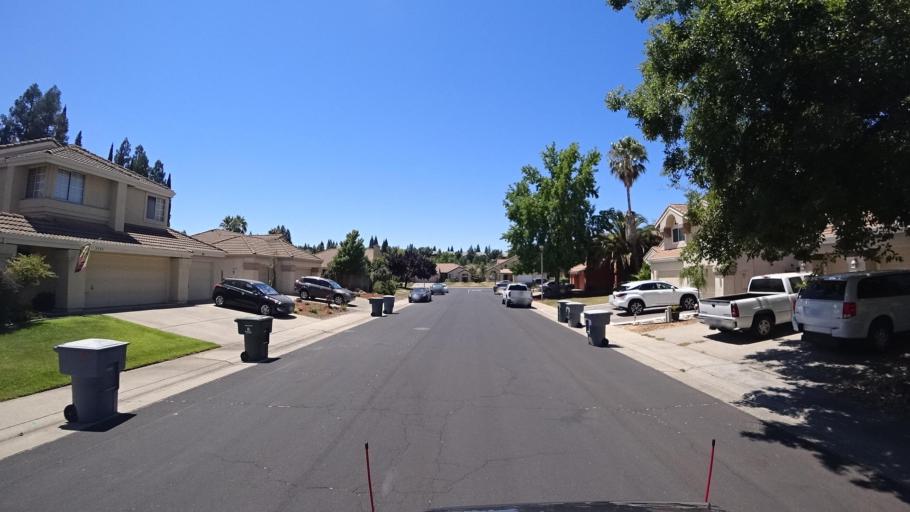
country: US
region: California
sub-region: Placer County
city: Rocklin
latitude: 38.8110
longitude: -121.2726
